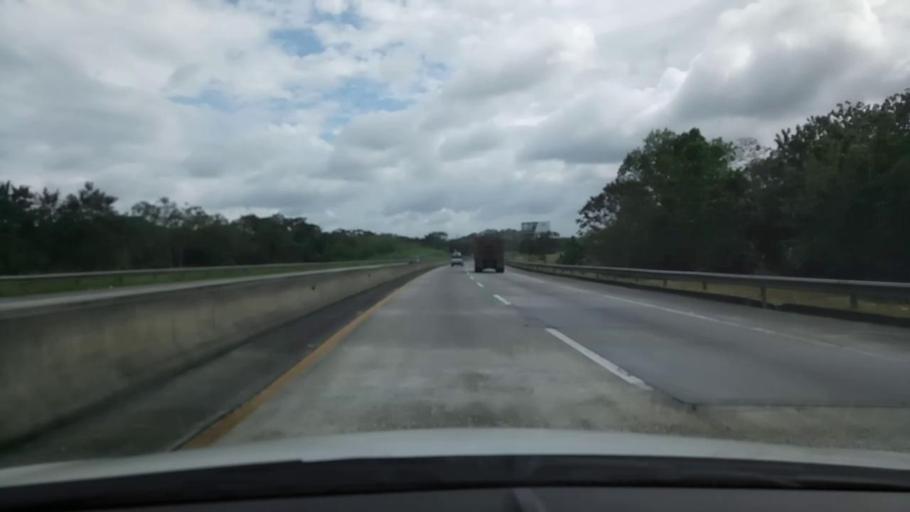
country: PA
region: Panama
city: Chilibre
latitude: 9.1836
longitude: -79.6399
